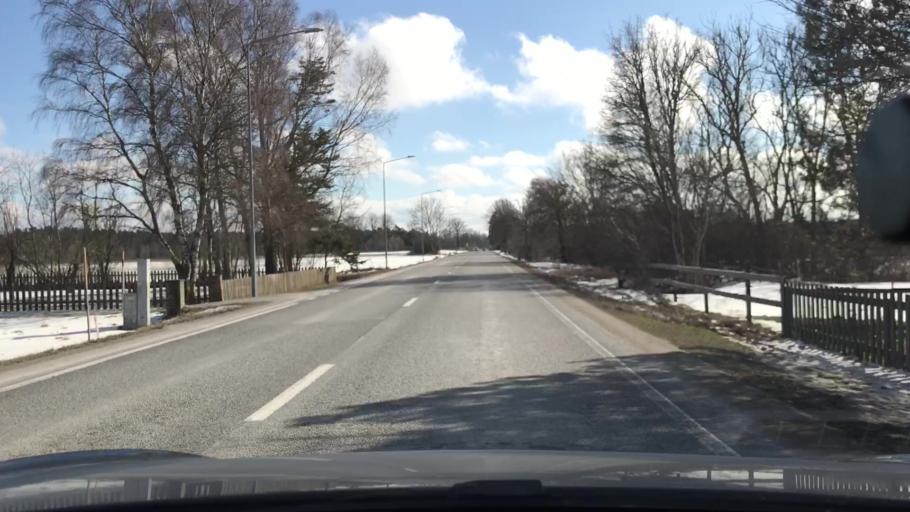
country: SE
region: Gotland
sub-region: Gotland
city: Visby
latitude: 57.5261
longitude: 18.4405
